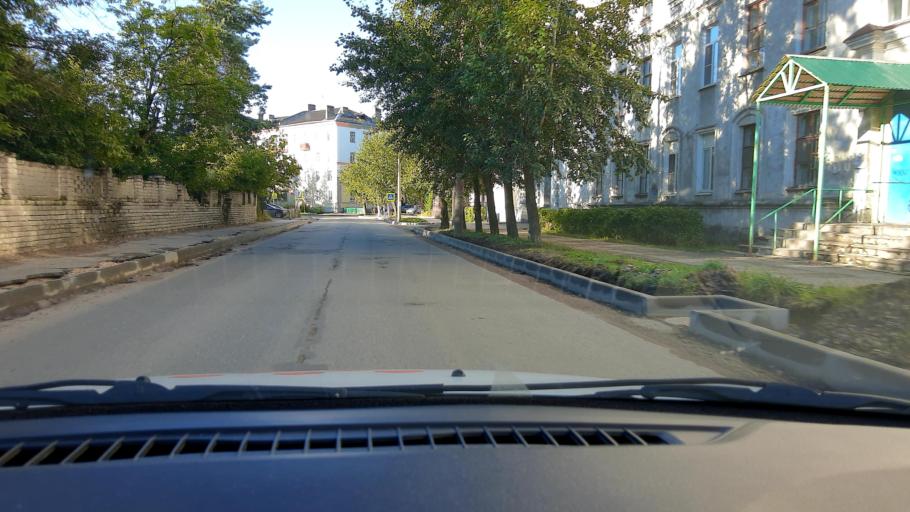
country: RU
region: Nizjnij Novgorod
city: Dzerzhinsk
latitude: 56.2447
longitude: 43.4717
